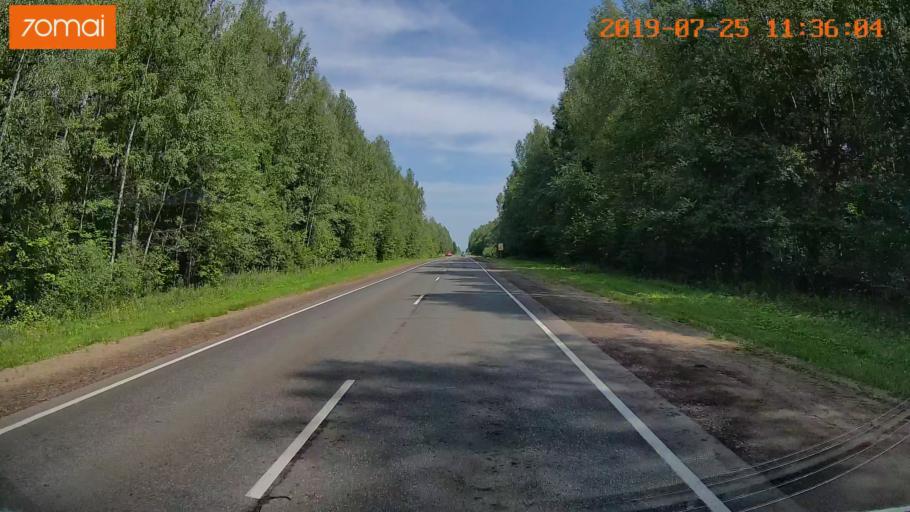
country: RU
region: Ivanovo
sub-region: Privolzhskiy Rayon
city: Ples
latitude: 57.4189
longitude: 41.4414
